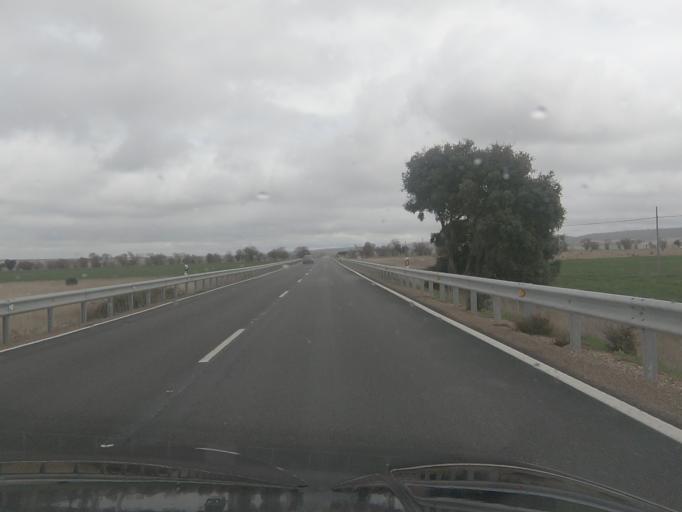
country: ES
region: Castille and Leon
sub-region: Provincia de Zamora
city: Pozuelo de Tabara
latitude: 41.7968
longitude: -5.9130
